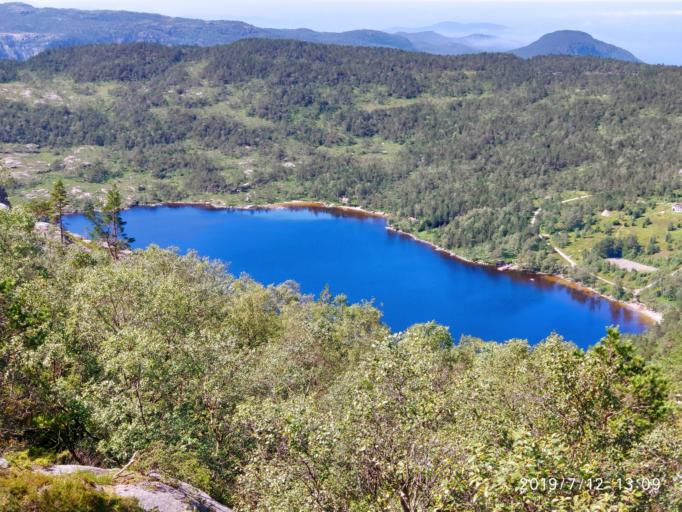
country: NO
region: Rogaland
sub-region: Forsand
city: Forsand
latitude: 58.9886
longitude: 6.1523
